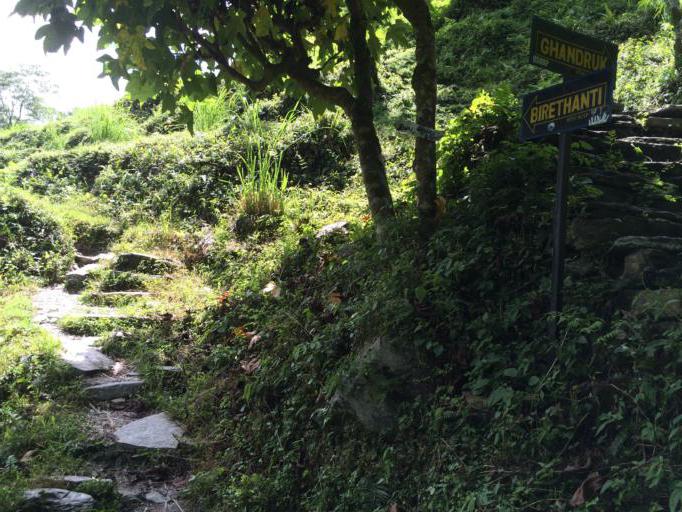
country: NP
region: Western Region
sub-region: Dhawalagiri Zone
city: Chitre
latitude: 28.3725
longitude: 83.8182
